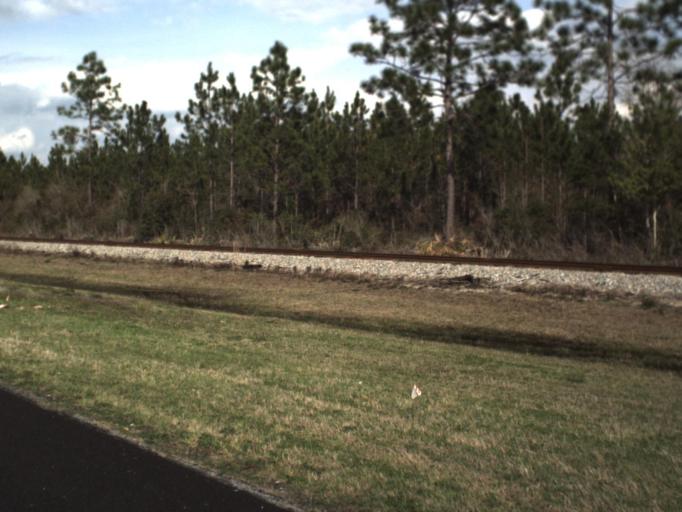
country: US
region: Florida
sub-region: Bay County
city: Youngstown
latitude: 30.4205
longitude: -85.4295
